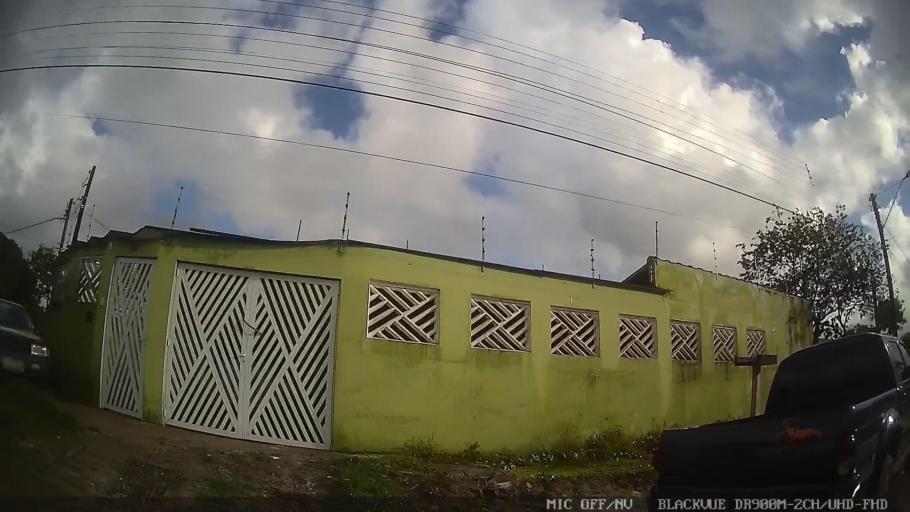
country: BR
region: Sao Paulo
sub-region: Itanhaem
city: Itanhaem
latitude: -24.1751
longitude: -46.8502
